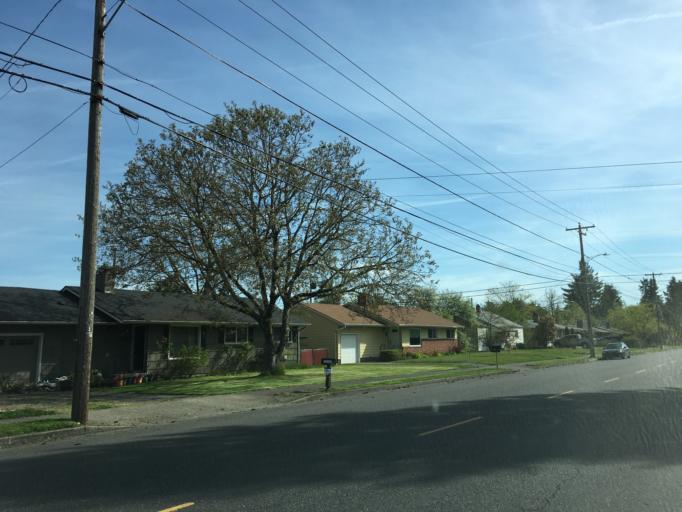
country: US
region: Oregon
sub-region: Multnomah County
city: Lents
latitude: 45.5372
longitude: -122.5305
